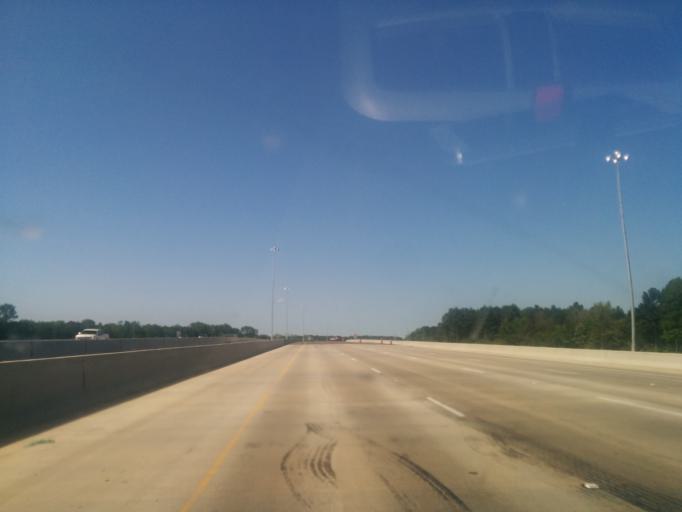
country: US
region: Mississippi
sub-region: Madison County
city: Ridgeland
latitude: 32.4460
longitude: -90.1446
